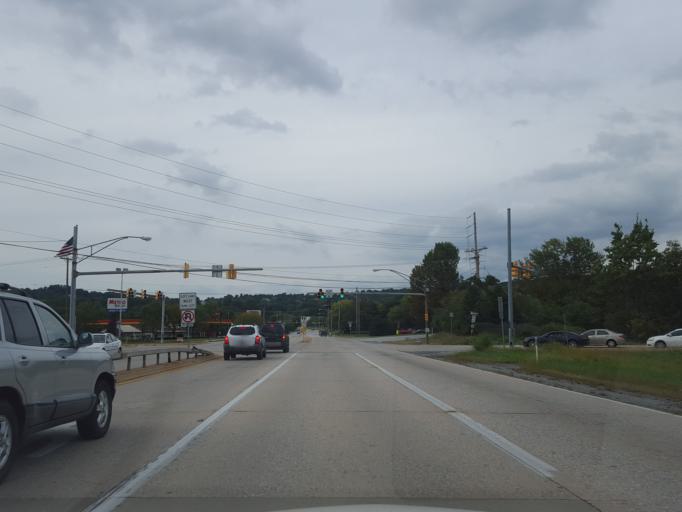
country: US
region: Pennsylvania
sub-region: York County
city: Yorklyn
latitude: 39.9875
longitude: -76.6683
